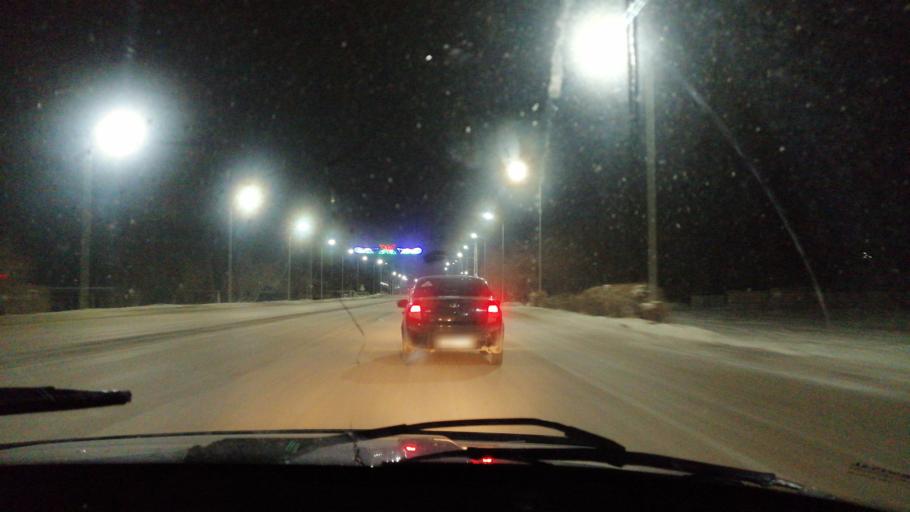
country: KZ
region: Aqtoebe
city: Aqtobe
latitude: 50.2949
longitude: 57.1930
